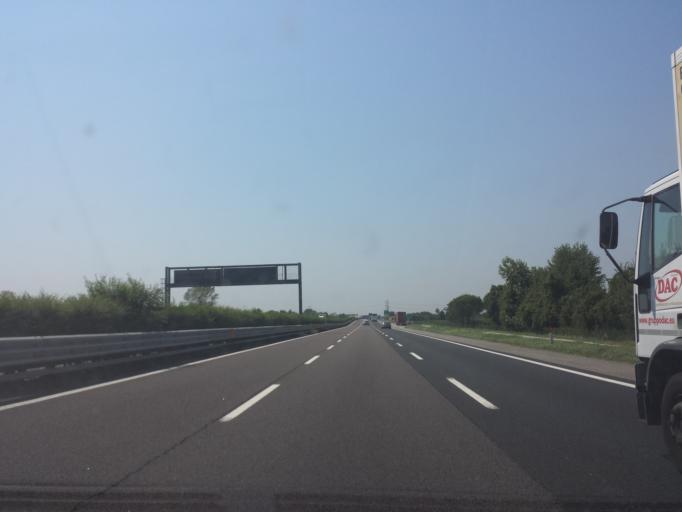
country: IT
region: Veneto
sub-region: Provincia di Venezia
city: Marano
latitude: 45.4600
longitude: 12.1410
